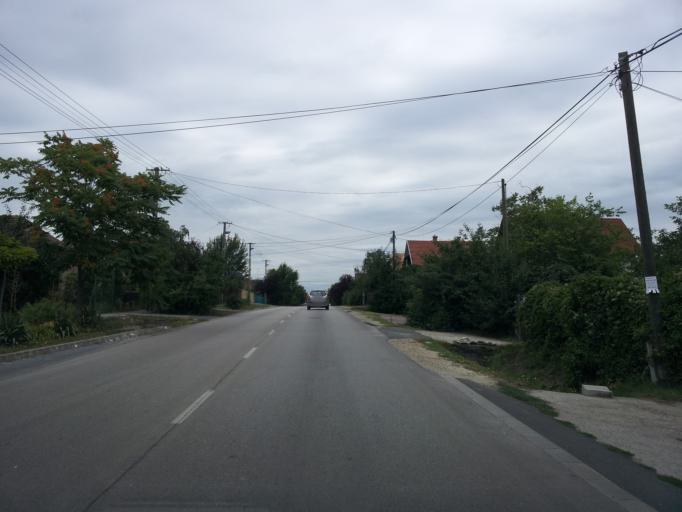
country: HU
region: Pest
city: Erd
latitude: 47.3987
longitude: 18.8908
